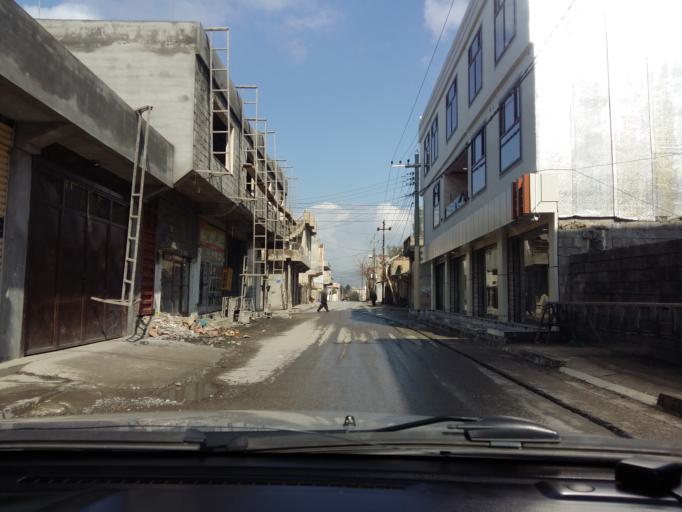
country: IQ
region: As Sulaymaniyah
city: Qeladize
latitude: 36.1788
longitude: 45.1218
